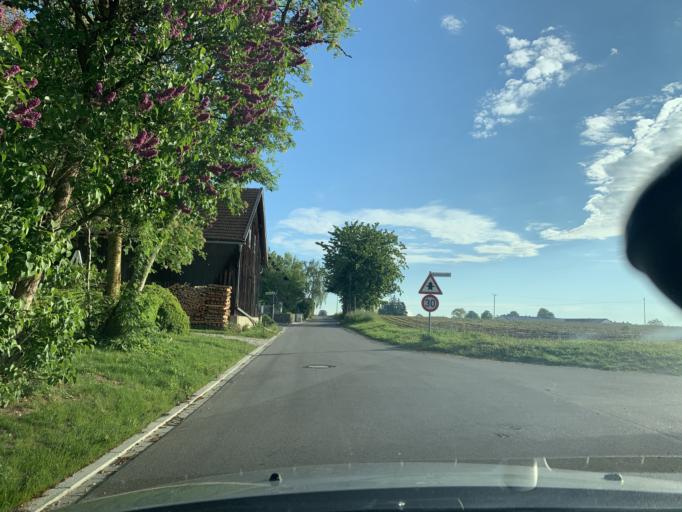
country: DE
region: Bavaria
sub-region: Lower Bavaria
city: Stallwang
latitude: 48.5154
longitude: 12.2226
